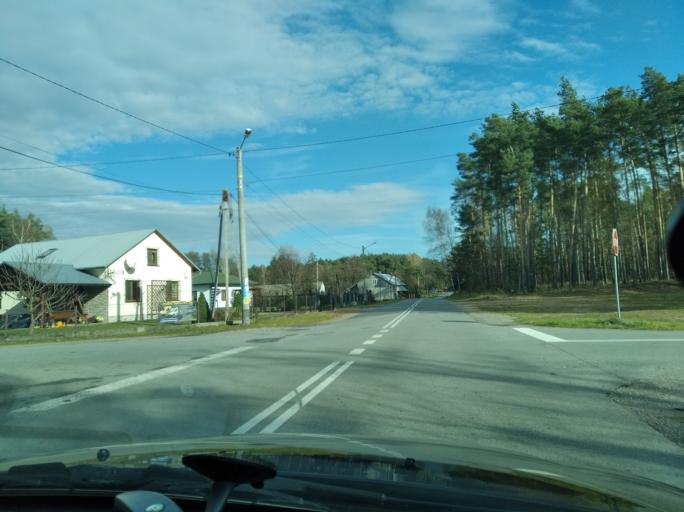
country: PL
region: Subcarpathian Voivodeship
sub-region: Powiat ropczycko-sedziszowski
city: Sedziszow Malopolski
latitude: 50.1143
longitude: 21.6897
